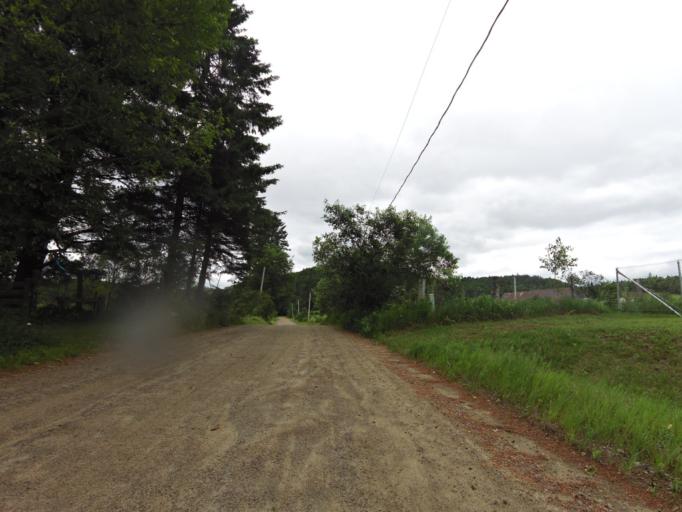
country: CA
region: Quebec
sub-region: Laurentides
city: Mont-Tremblant
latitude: 45.9147
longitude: -74.6532
